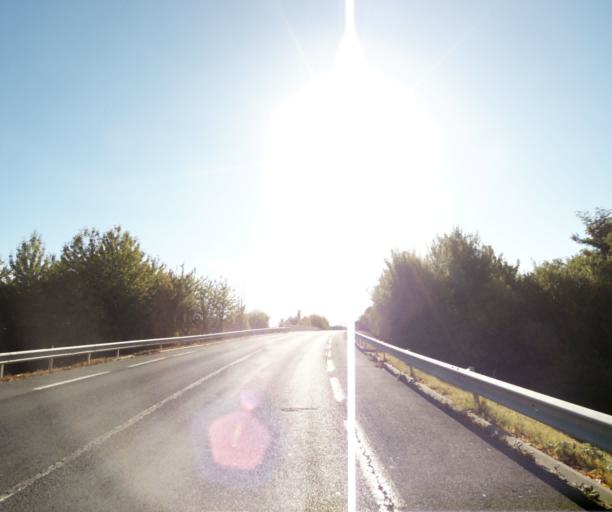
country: FR
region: Auvergne
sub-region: Departement du Puy-de-Dome
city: Malintrat
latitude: 45.8159
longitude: 3.1737
